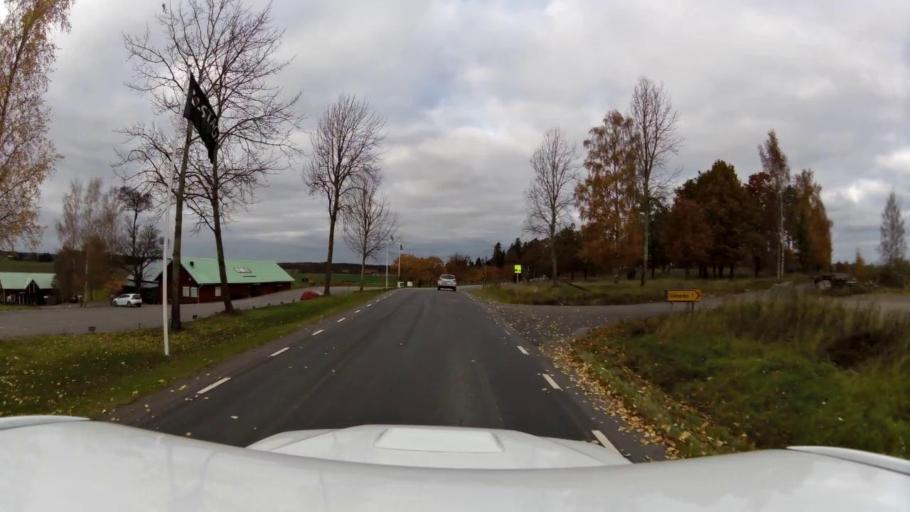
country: SE
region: OEstergoetland
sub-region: Linkopings Kommun
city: Linghem
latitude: 58.4124
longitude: 15.7502
